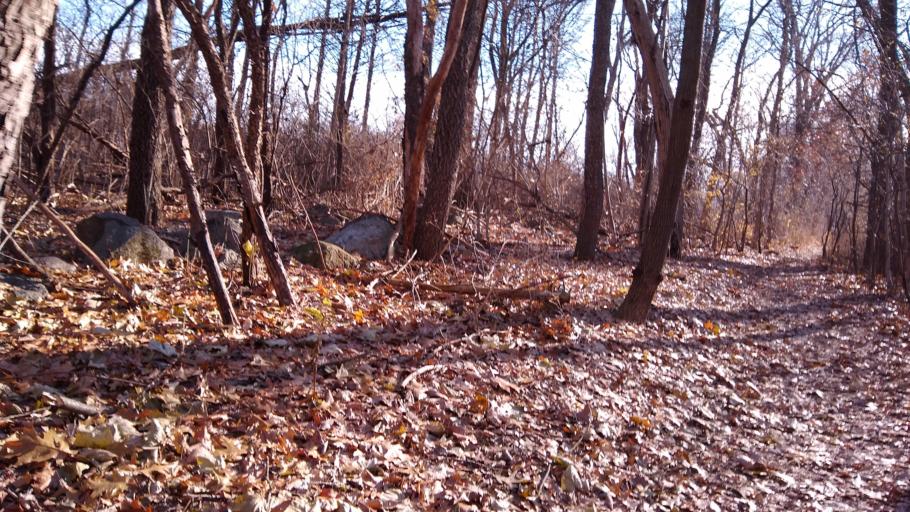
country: US
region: Wisconsin
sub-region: Dane County
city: Shorewood Hills
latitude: 43.0429
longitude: -89.4330
